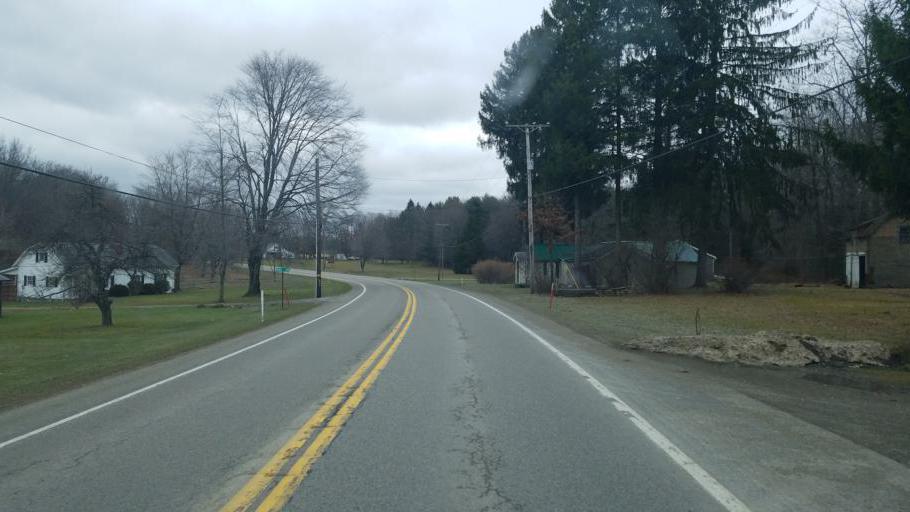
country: US
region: Pennsylvania
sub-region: Forest County
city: Marienville
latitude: 41.3896
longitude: -79.2661
